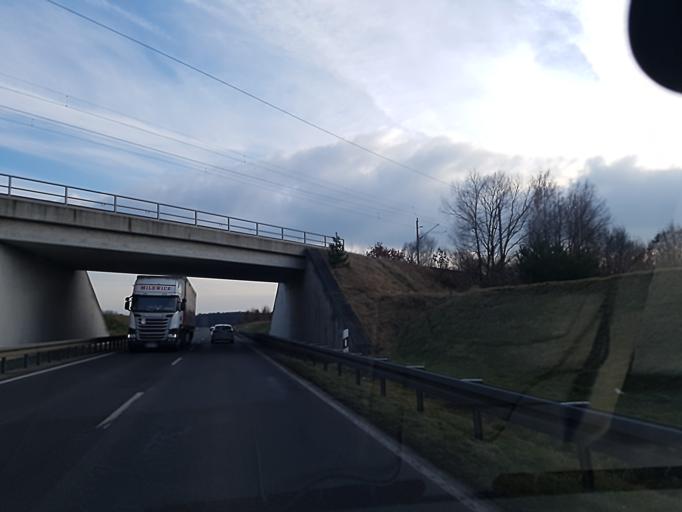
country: DE
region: Brandenburg
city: Belzig
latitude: 52.1431
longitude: 12.6213
